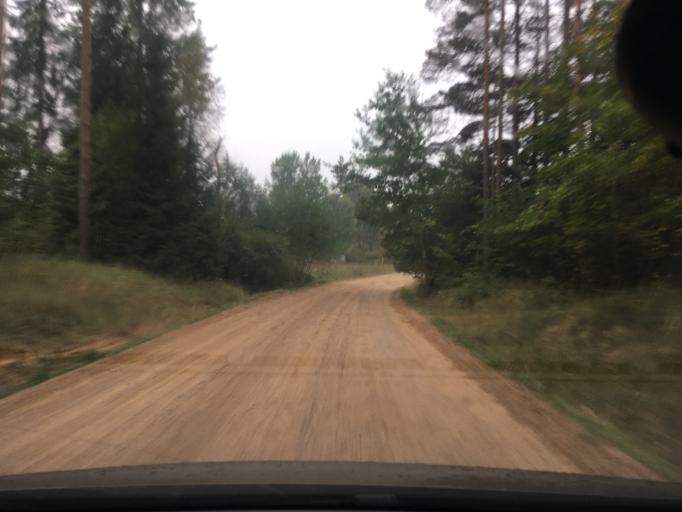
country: LV
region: Kuldigas Rajons
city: Kuldiga
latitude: 57.0107
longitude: 21.9831
